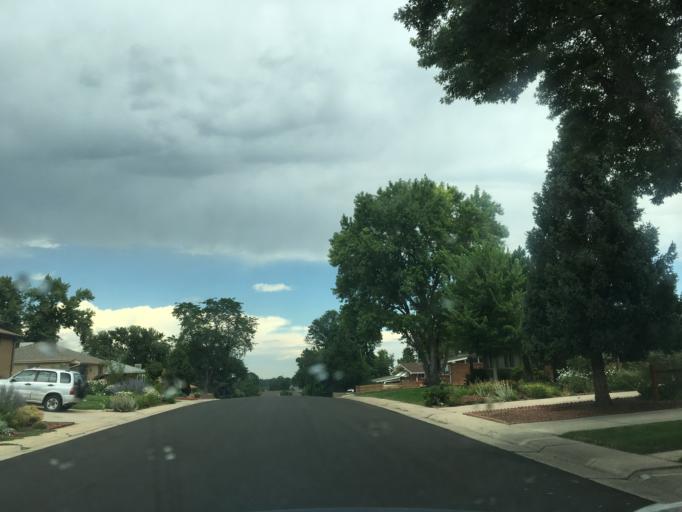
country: US
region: Colorado
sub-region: Arapahoe County
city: Sheridan
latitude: 39.6745
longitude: -105.0469
